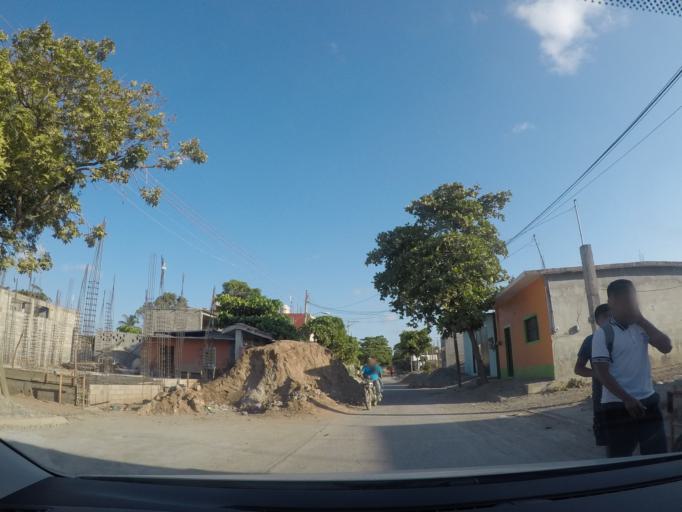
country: MX
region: Oaxaca
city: Juchitan de Zaragoza
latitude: 16.4382
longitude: -95.0289
